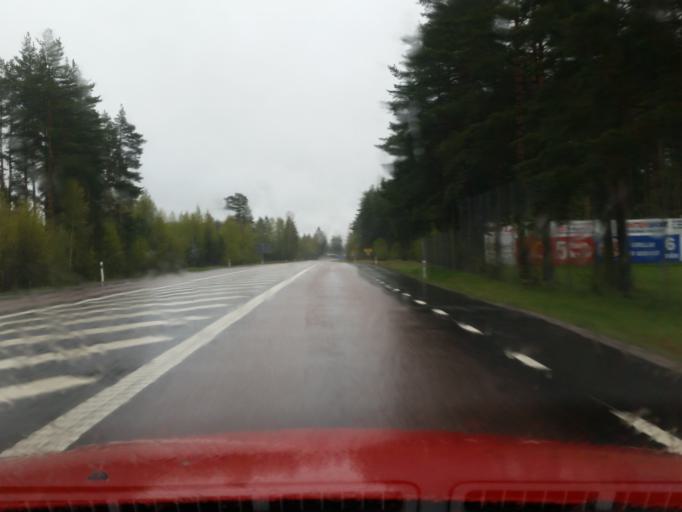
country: SE
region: Dalarna
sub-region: Borlange Kommun
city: Borlaenge
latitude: 60.5289
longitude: 15.3361
